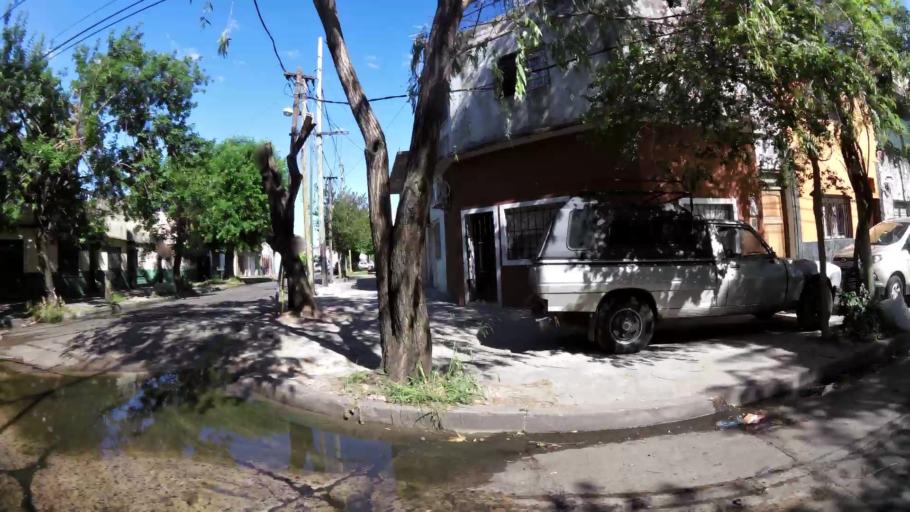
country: AR
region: Buenos Aires
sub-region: Partido de General San Martin
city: General San Martin
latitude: -34.5276
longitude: -58.5747
